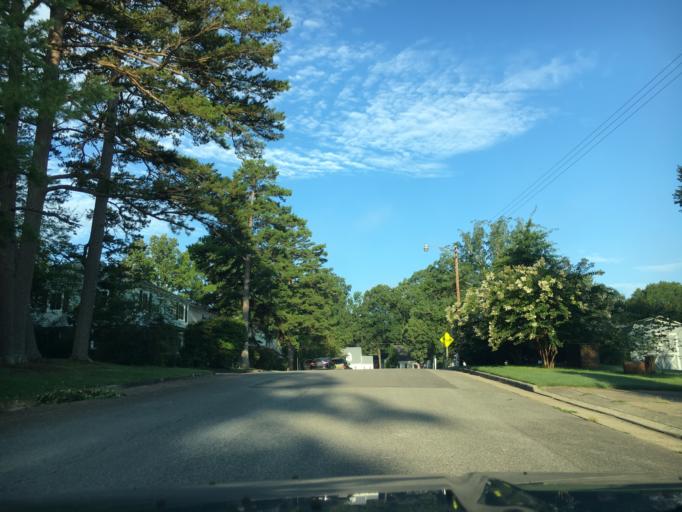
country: US
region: Virginia
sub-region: Halifax County
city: South Boston
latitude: 36.7036
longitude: -78.8931
